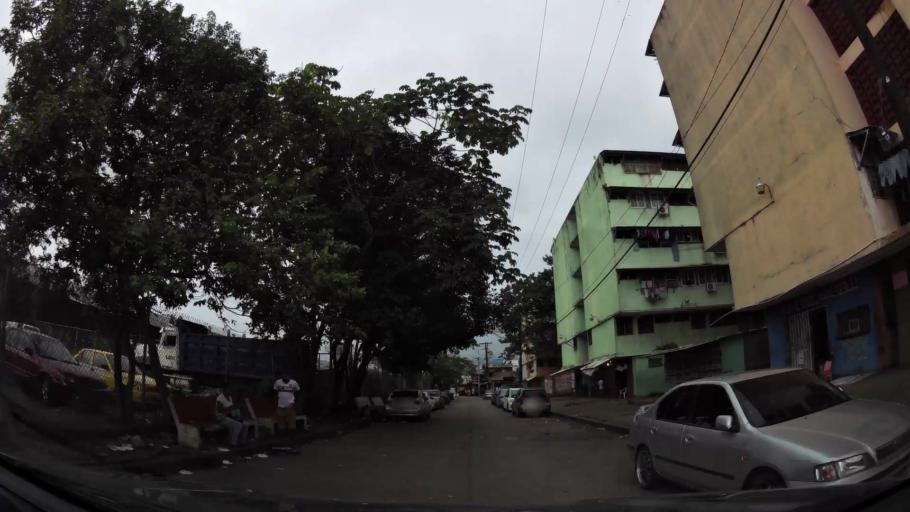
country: PA
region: Panama
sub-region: Distrito de Panama
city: Ancon
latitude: 8.9667
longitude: -79.5449
